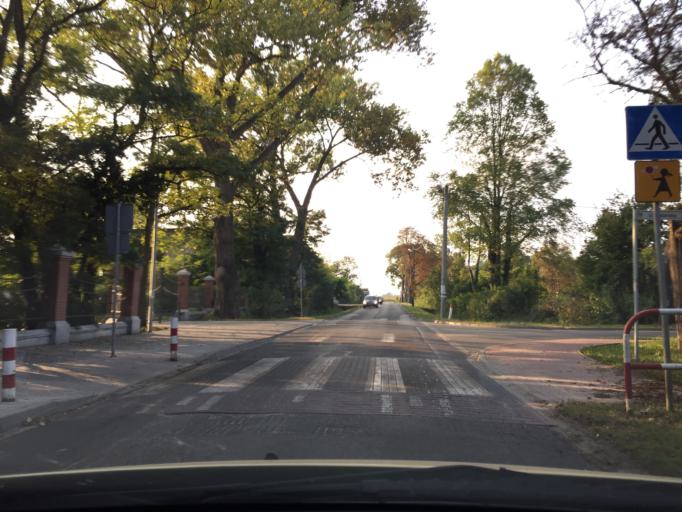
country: PL
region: Greater Poland Voivodeship
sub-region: Powiat poznanski
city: Plewiska
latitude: 52.3695
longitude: 16.8056
